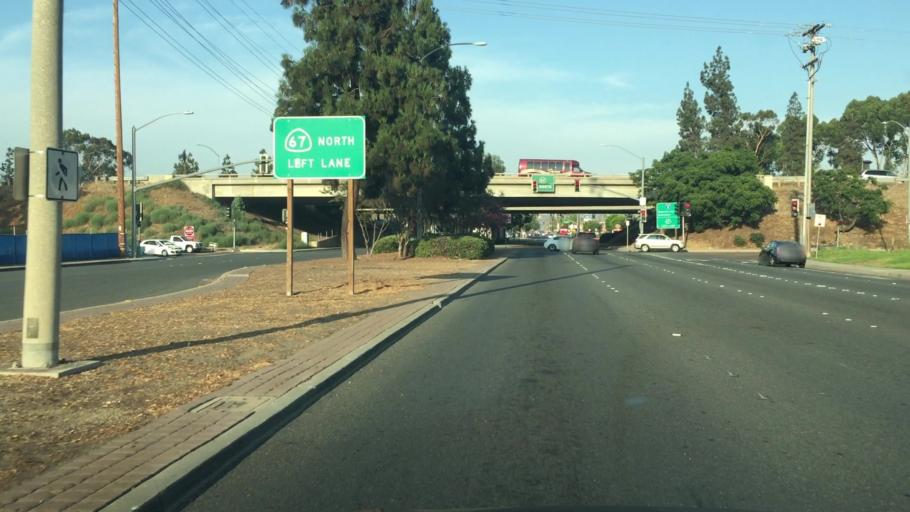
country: US
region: California
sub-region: San Diego County
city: El Cajon
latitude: 32.8077
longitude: -116.9634
